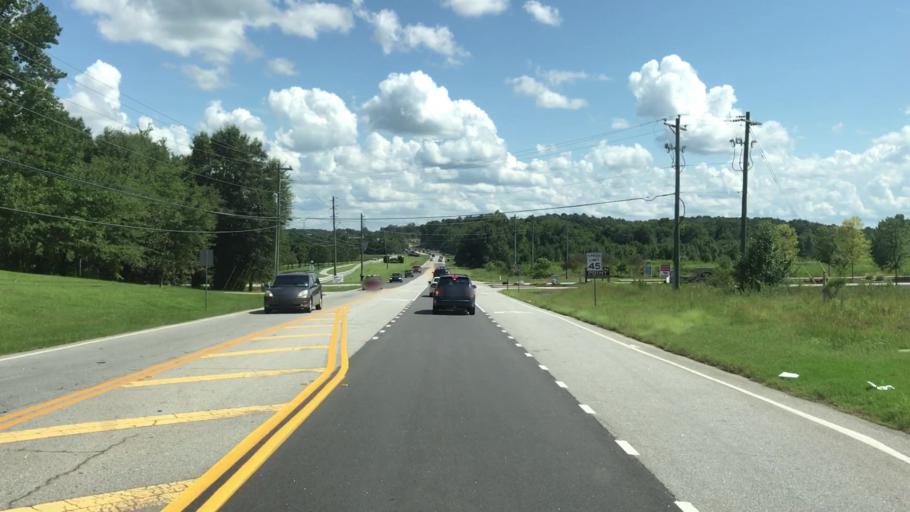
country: US
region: Georgia
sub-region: Walton County
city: Loganville
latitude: 33.8269
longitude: -83.8786
